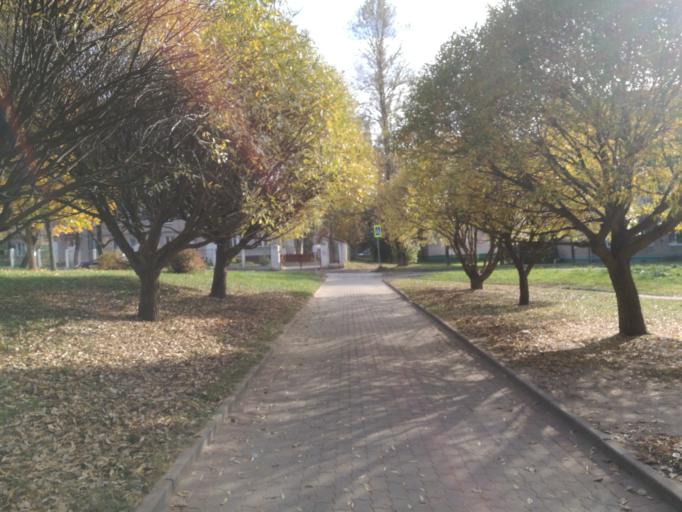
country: BY
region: Minsk
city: Minsk
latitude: 53.8966
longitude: 27.5172
